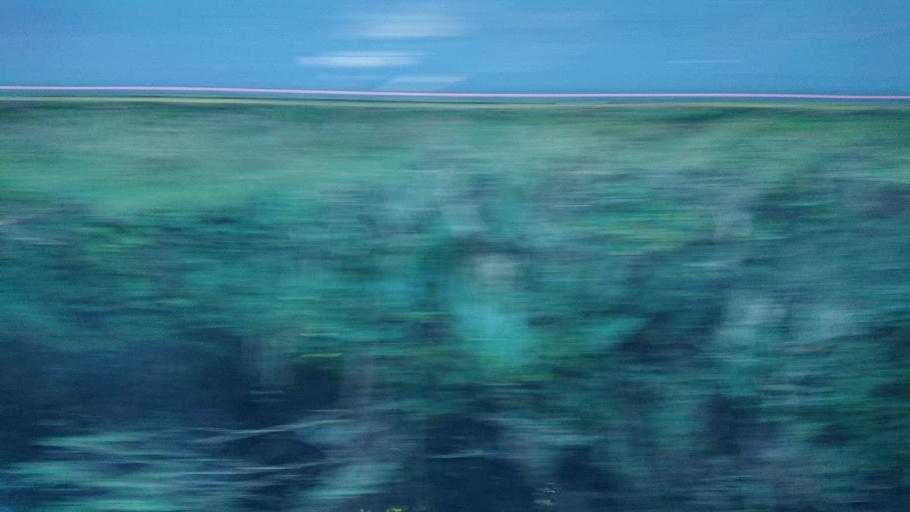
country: TW
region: Taiwan
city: Lugu
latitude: 23.5048
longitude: 120.7973
